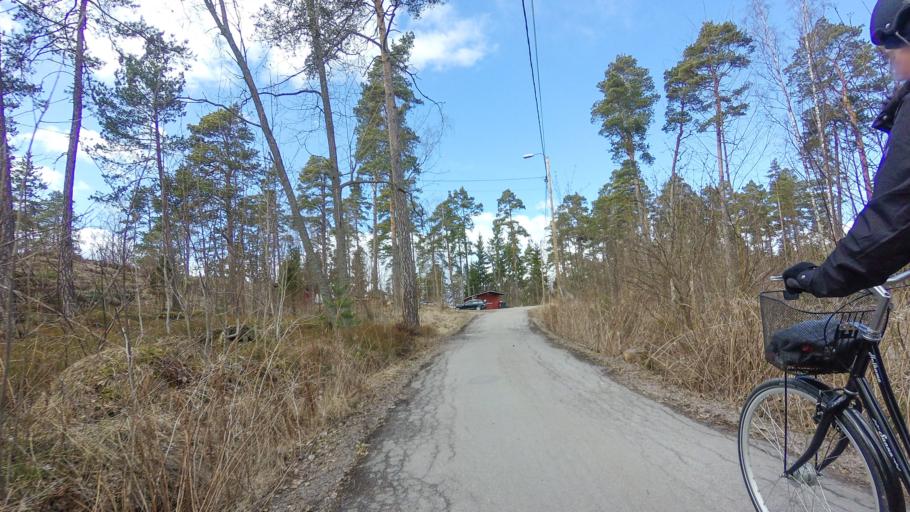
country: FI
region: Uusimaa
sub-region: Helsinki
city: Vantaa
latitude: 60.1886
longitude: 25.0919
